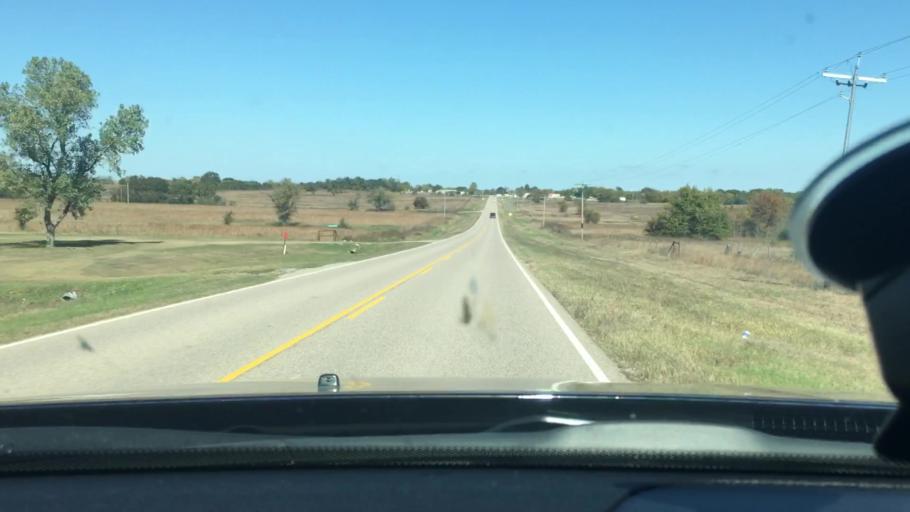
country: US
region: Oklahoma
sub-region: Johnston County
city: Tishomingo
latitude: 34.4334
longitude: -96.6360
